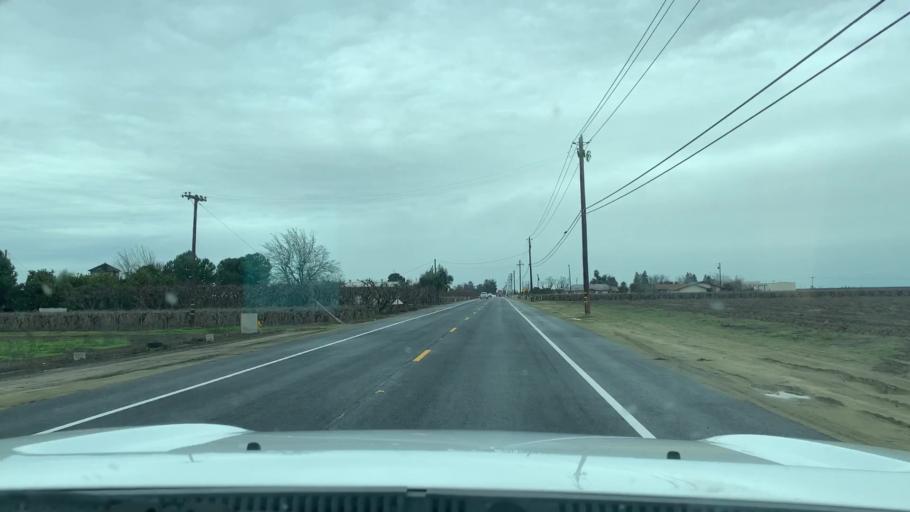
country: US
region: California
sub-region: Fresno County
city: Fowler
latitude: 36.6006
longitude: -119.6824
